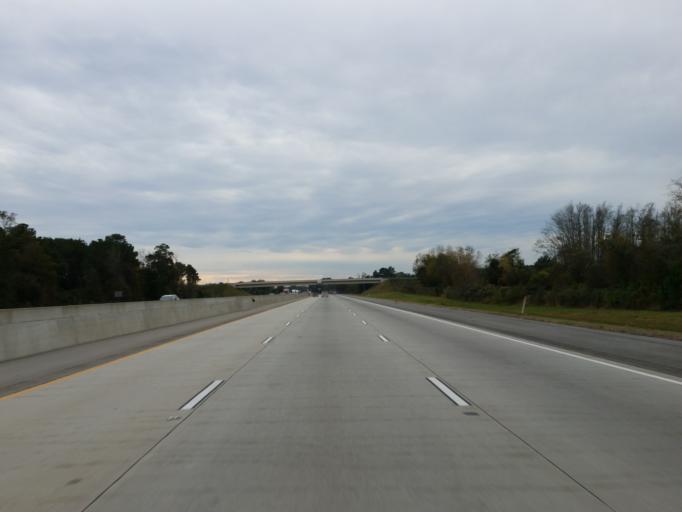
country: US
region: Georgia
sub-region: Tift County
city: Omega
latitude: 31.2974
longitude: -83.4774
